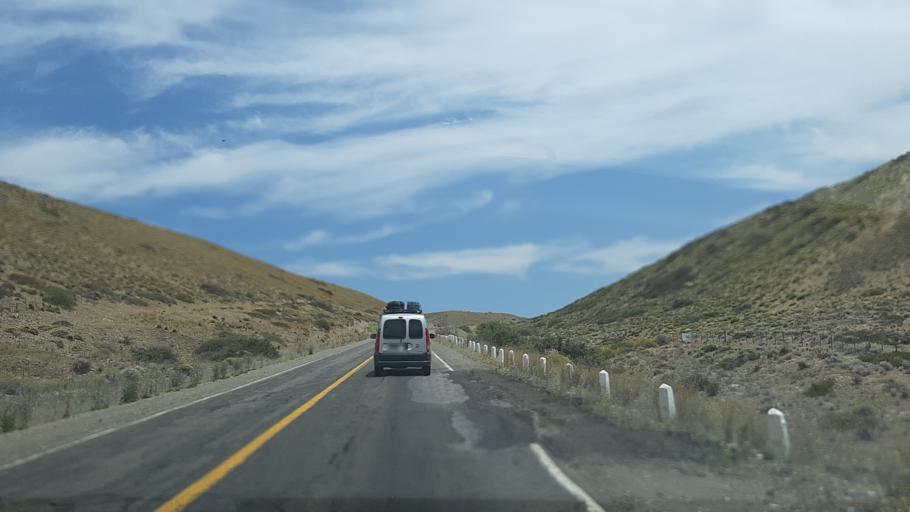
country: AR
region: Rio Negro
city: Pilcaniyeu
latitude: -40.4809
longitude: -70.6716
